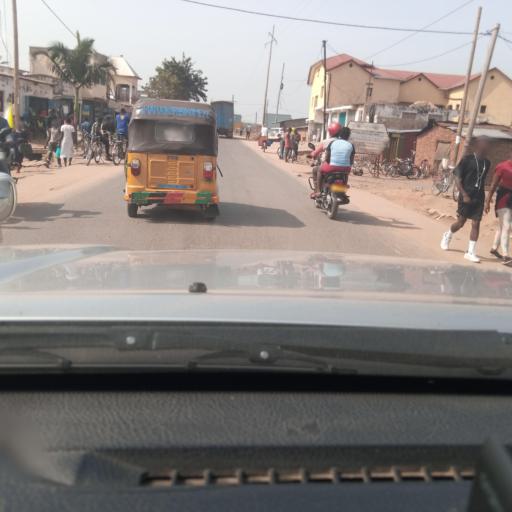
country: BI
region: Bujumbura Mairie
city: Bujumbura
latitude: -3.4352
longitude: 29.3541
